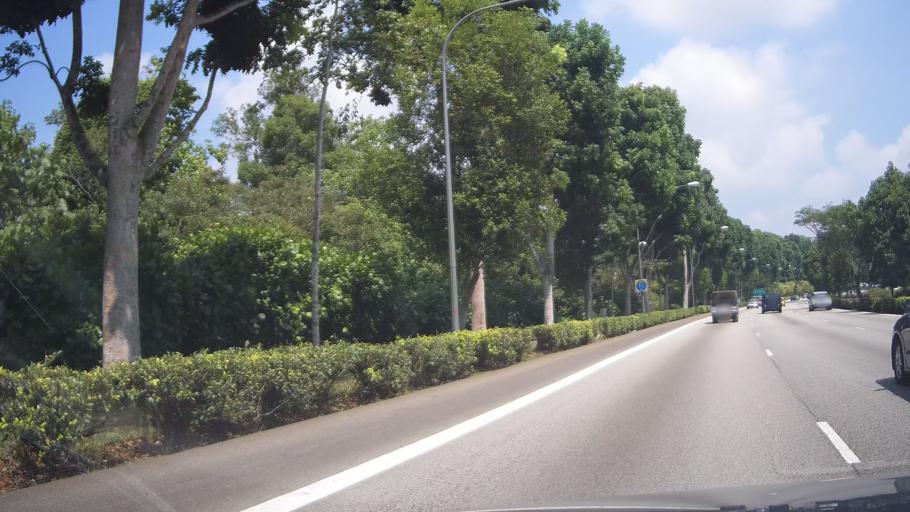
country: SG
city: Singapore
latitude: 1.3580
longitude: 103.7822
